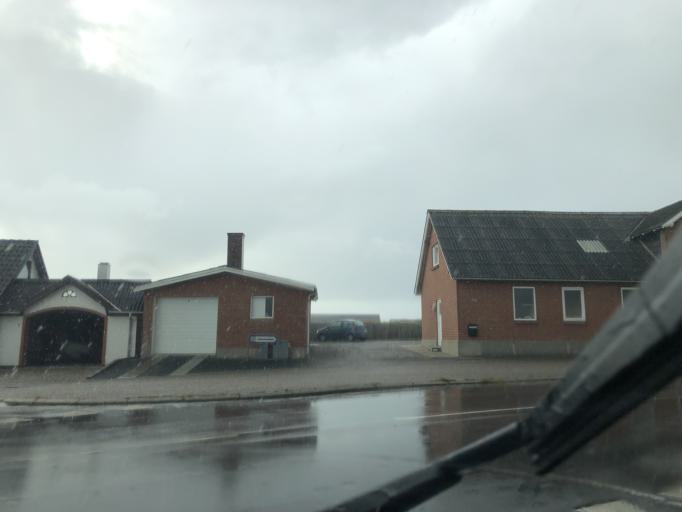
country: DK
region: Central Jutland
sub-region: Lemvig Kommune
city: Harboore
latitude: 56.5257
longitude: 8.1233
